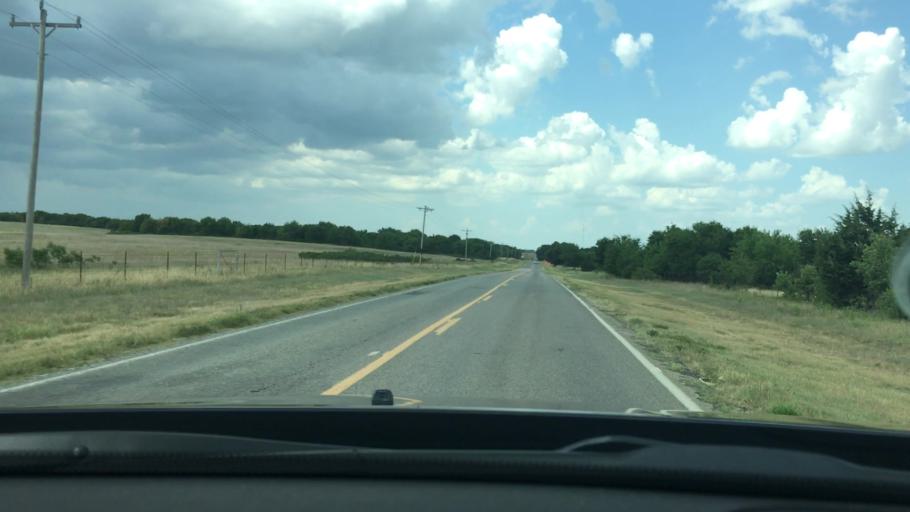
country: US
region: Oklahoma
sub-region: Pontotoc County
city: Ada
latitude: 34.5399
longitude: -96.6346
